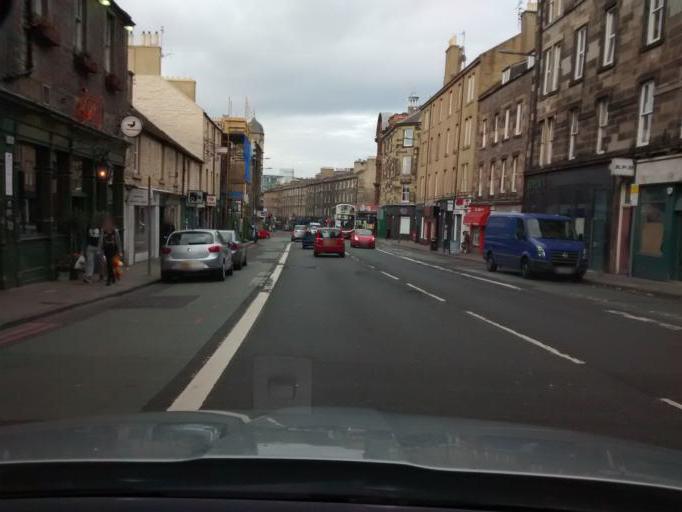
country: GB
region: Scotland
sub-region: Edinburgh
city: Edinburgh
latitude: 55.9409
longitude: -3.2036
